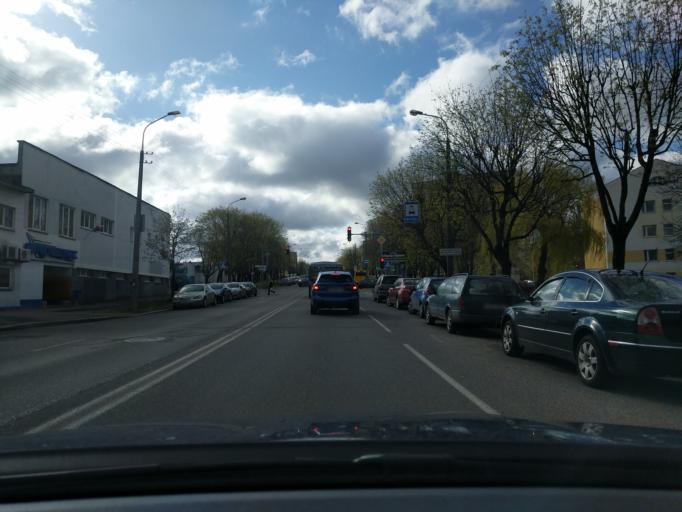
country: BY
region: Minsk
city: Novoye Medvezhino
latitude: 53.9174
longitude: 27.5019
